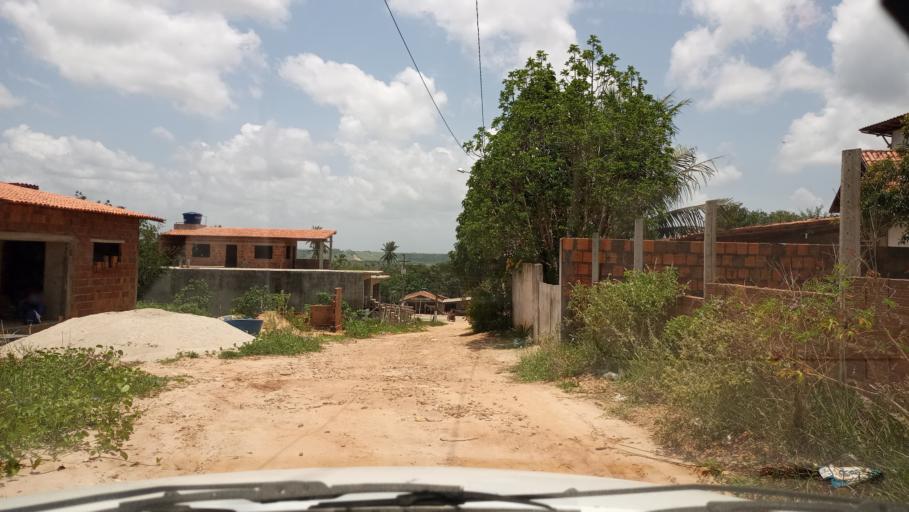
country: BR
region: Rio Grande do Norte
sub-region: Ares
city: Ares
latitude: -6.2335
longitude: -35.1463
